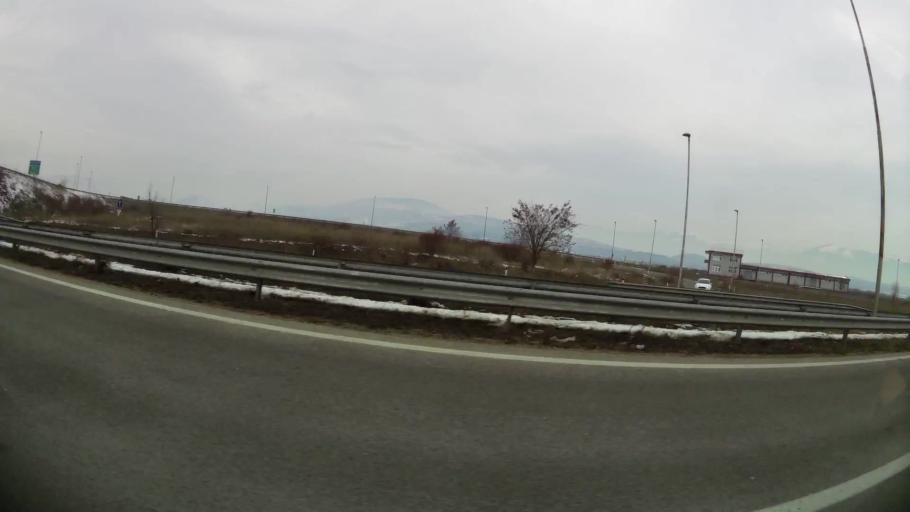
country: MK
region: Suto Orizari
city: Suto Orizare
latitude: 42.0530
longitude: 21.3826
